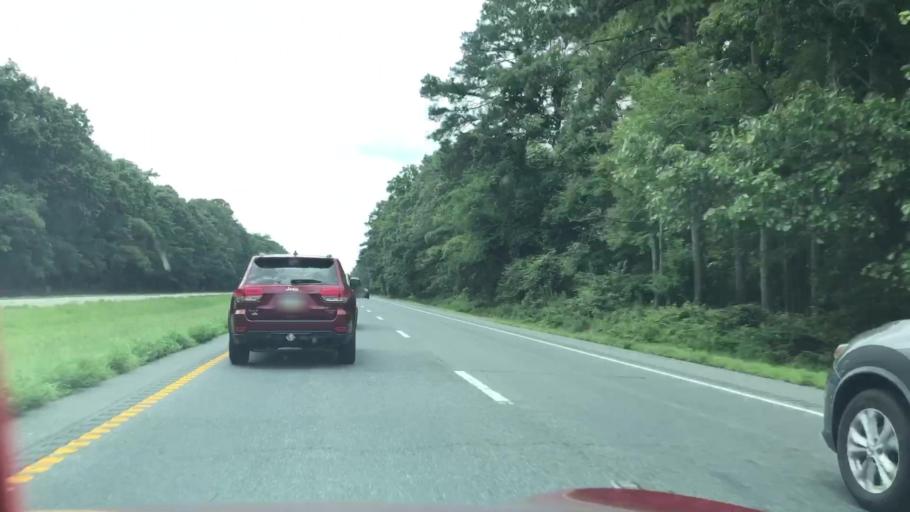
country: US
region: Virginia
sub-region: Northampton County
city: Eastville
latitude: 37.3590
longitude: -75.9344
